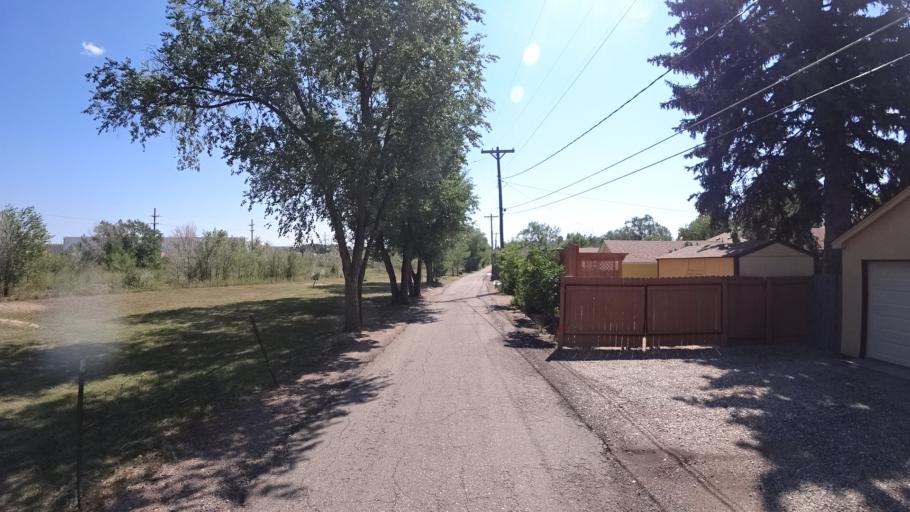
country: US
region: Colorado
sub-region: El Paso County
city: Colorado Springs
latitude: 38.8702
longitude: -104.8157
